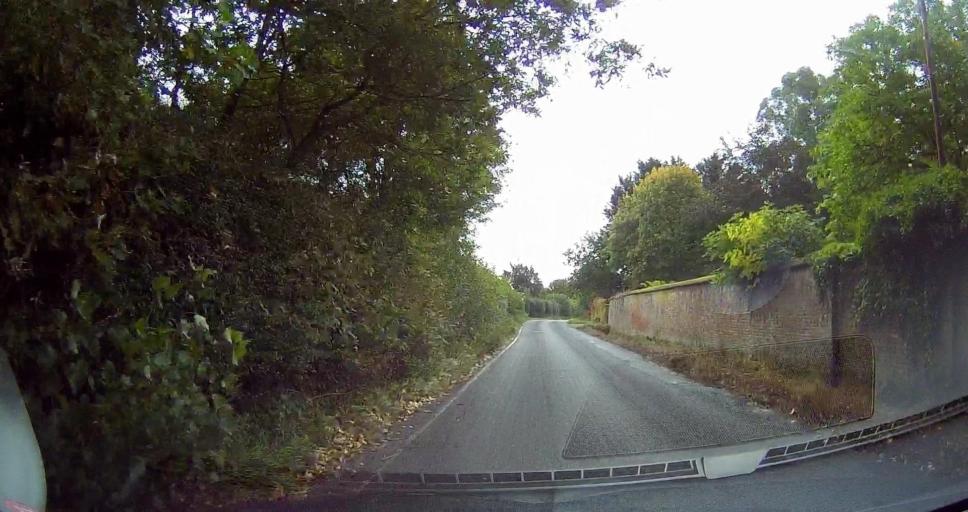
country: GB
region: England
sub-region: Kent
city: Hadlow
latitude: 51.2177
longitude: 0.3104
